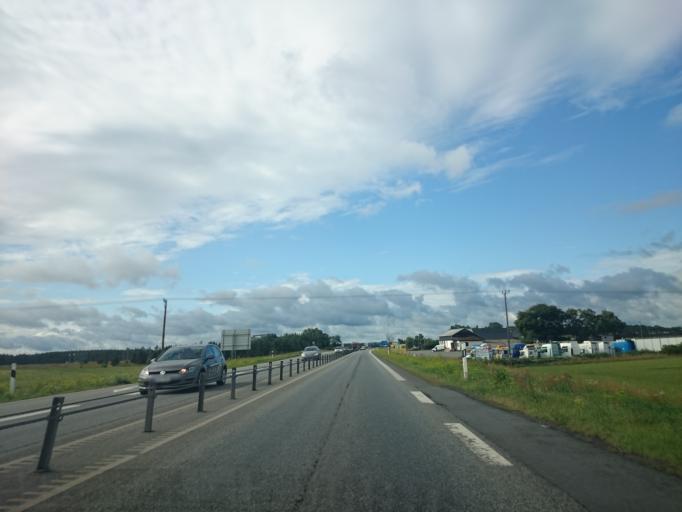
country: SE
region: Skane
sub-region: Kristianstads Kommun
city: Norra Asum
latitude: 55.9543
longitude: 14.0647
